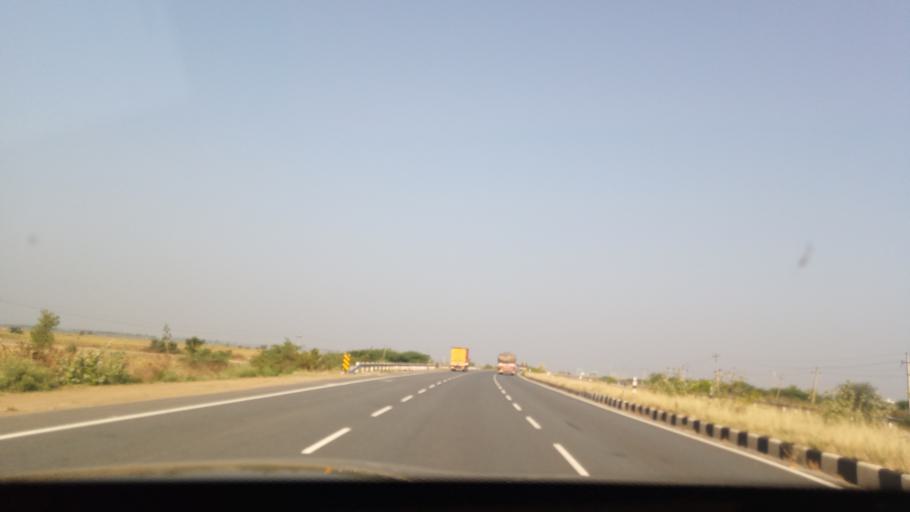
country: IN
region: Karnataka
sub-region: Haveri
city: Ranibennur
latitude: 14.5946
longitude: 75.6349
